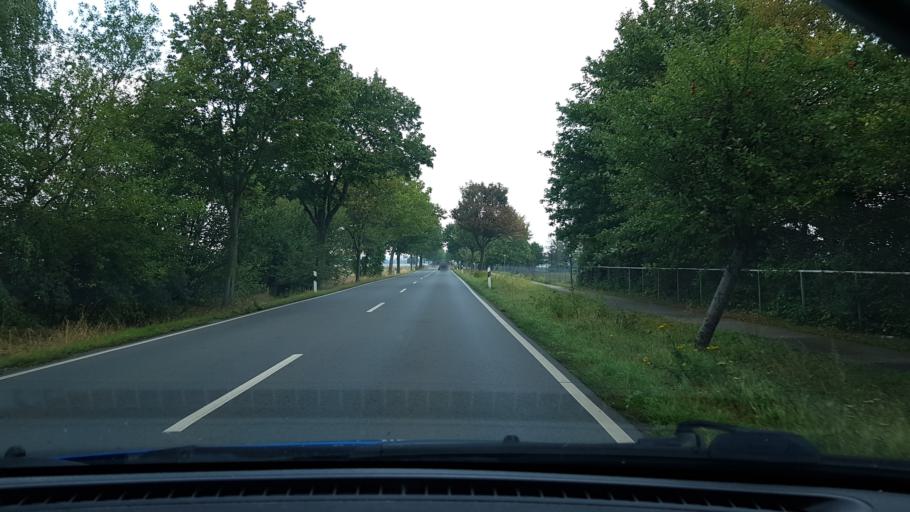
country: DE
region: Lower Saxony
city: Barsinghausen
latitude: 52.3122
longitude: 9.4620
